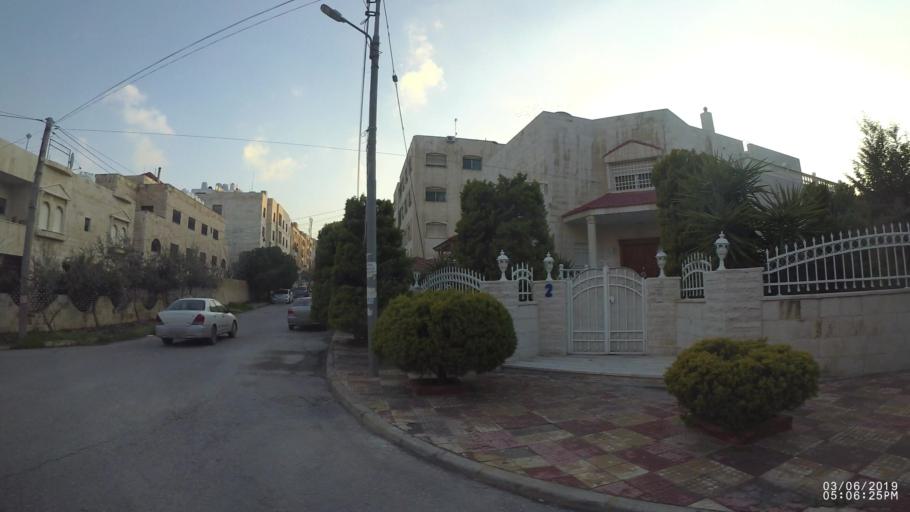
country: JO
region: Amman
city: Amman
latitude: 31.9925
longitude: 35.9468
